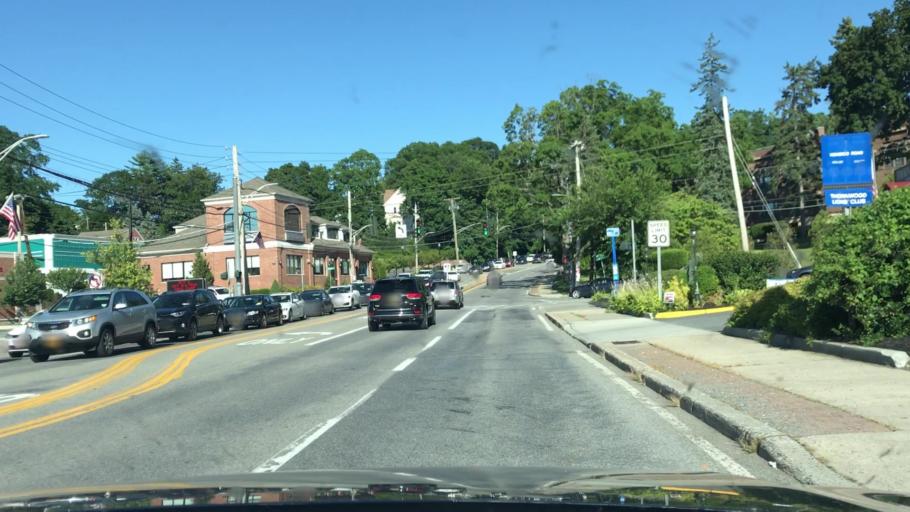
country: US
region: New York
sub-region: Westchester County
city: Thornwood
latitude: 41.1237
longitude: -73.7806
